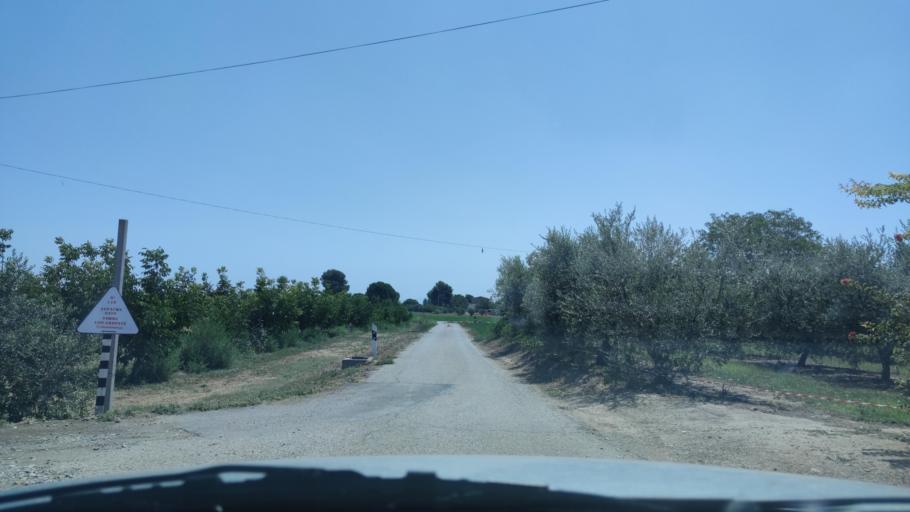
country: ES
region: Catalonia
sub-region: Provincia de Lleida
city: Torrefarrera
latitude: 41.6481
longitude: 0.5870
